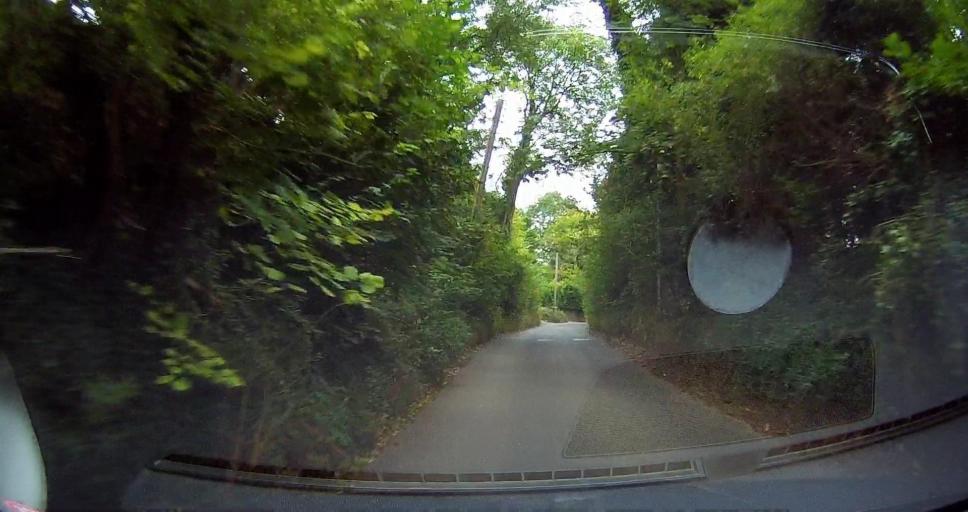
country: GB
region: England
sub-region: Kent
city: Longfield
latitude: 51.3597
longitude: 0.2838
